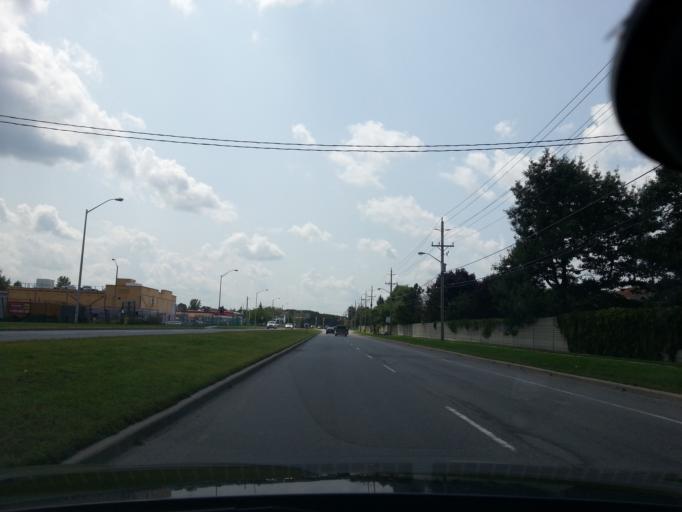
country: CA
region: Ontario
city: Ottawa
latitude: 45.3445
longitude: -75.6676
